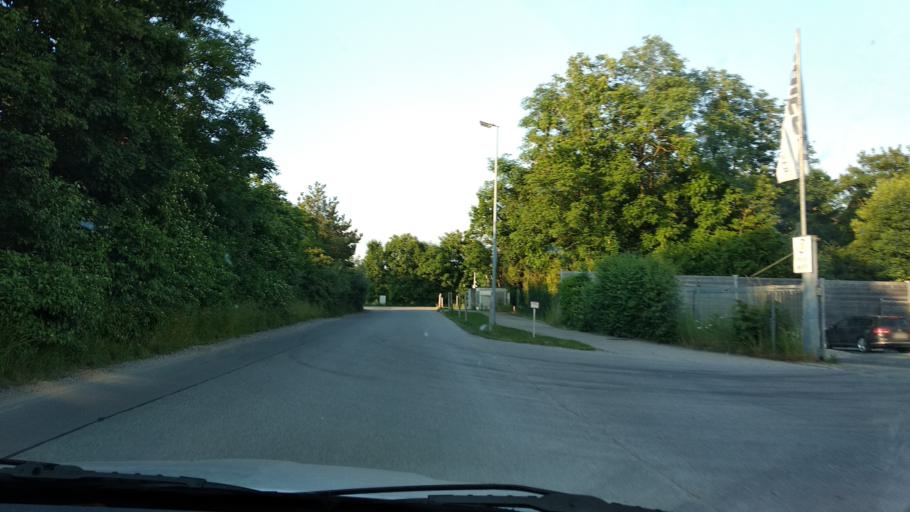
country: DE
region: Baden-Wuerttemberg
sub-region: Tuebingen Region
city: Aitrach
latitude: 47.9303
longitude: 10.0960
